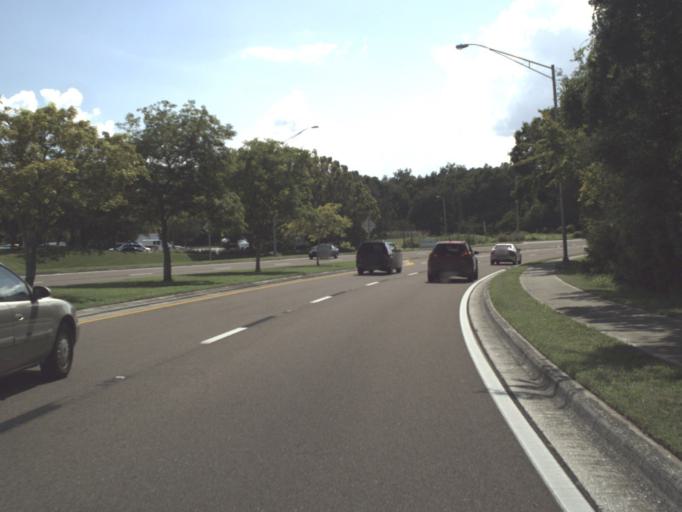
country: US
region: Florida
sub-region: Polk County
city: Lakeland
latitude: 28.0395
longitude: -81.9602
